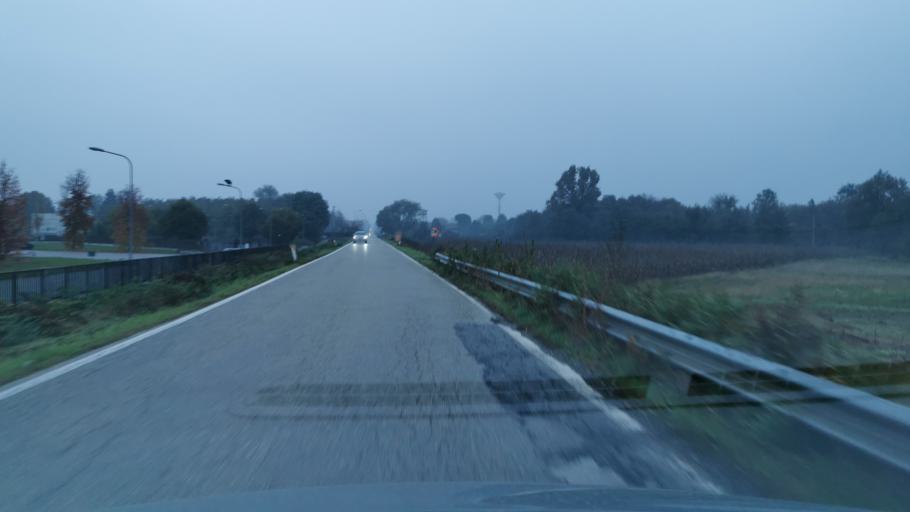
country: IT
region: Piedmont
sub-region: Provincia di Torino
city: Lusiglie
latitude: 45.3136
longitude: 7.7582
